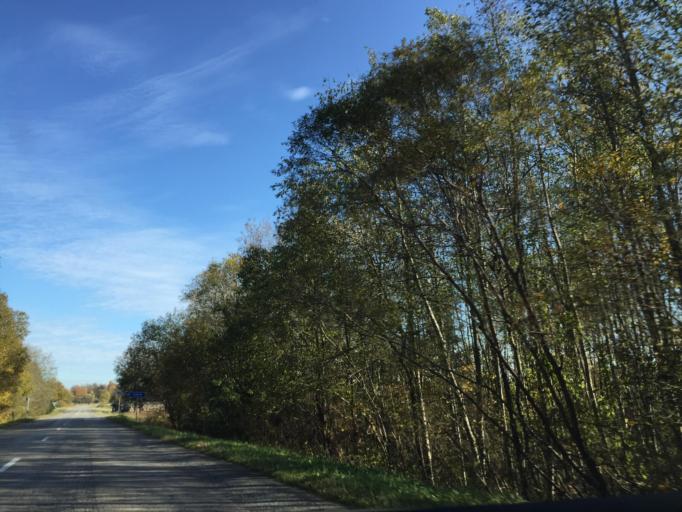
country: LV
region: Ogre
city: Jumprava
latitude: 56.7945
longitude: 25.0412
